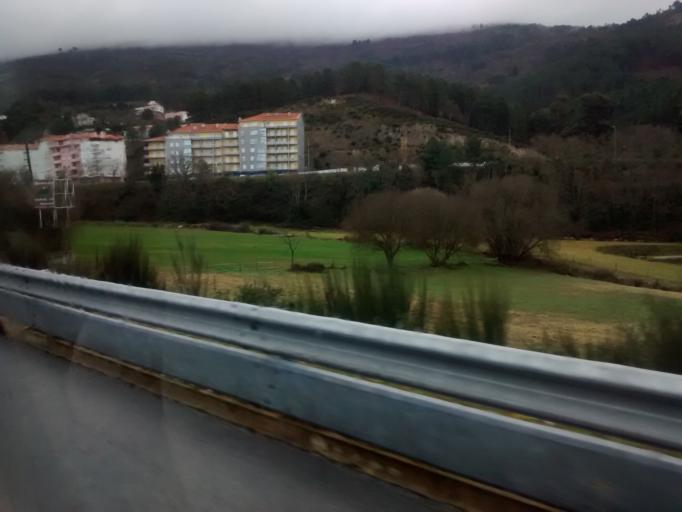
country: PT
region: Guarda
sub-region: Seia
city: Seia
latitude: 40.4096
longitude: -7.7102
